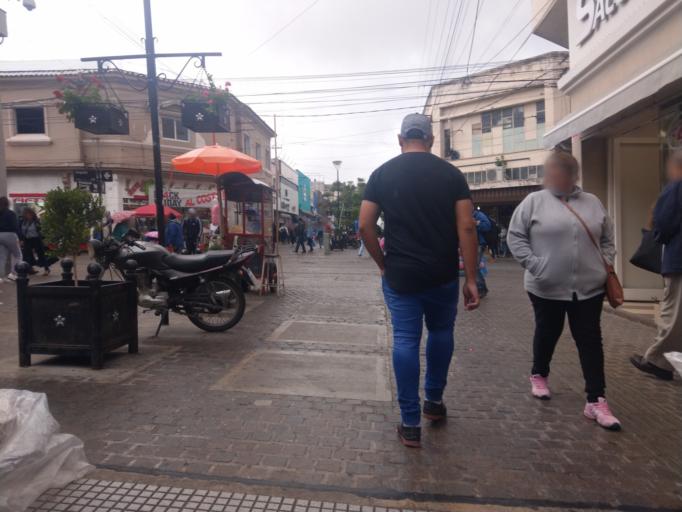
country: AR
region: Salta
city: Salta
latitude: -24.7921
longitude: -65.4127
